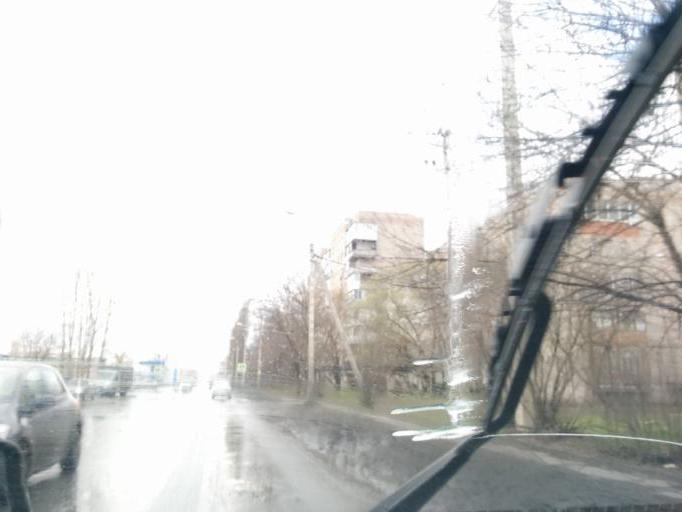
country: RU
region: Rostov
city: Shakhty
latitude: 47.6849
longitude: 40.2712
